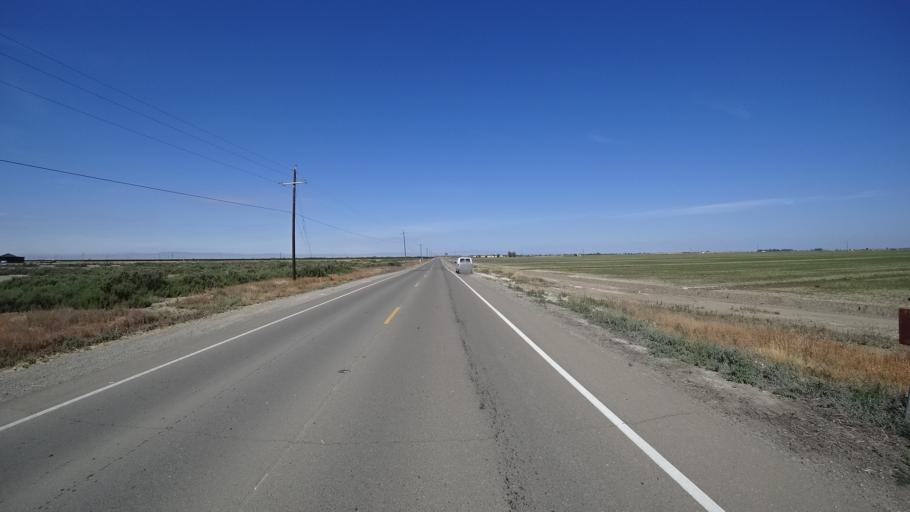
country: US
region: California
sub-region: Kings County
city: Lemoore
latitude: 36.2549
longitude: -119.8107
